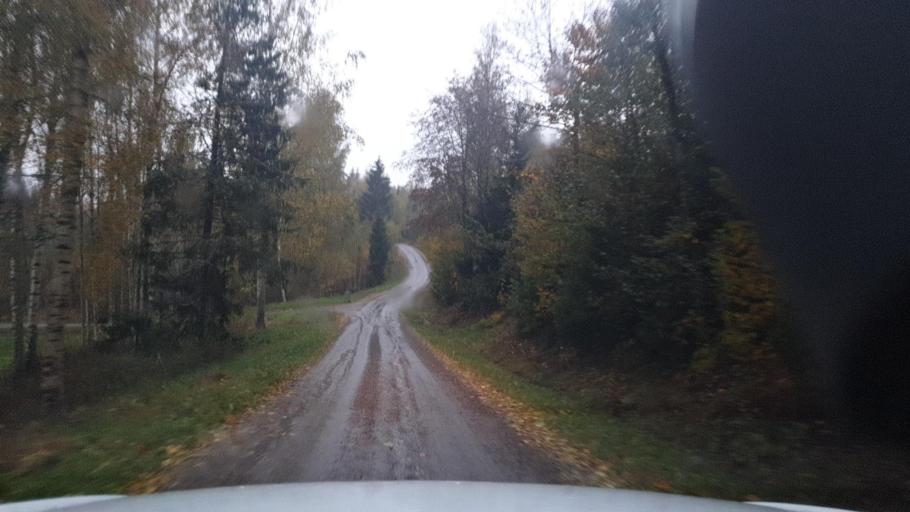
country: SE
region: Vaermland
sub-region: Eda Kommun
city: Amotfors
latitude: 59.8152
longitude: 12.4186
